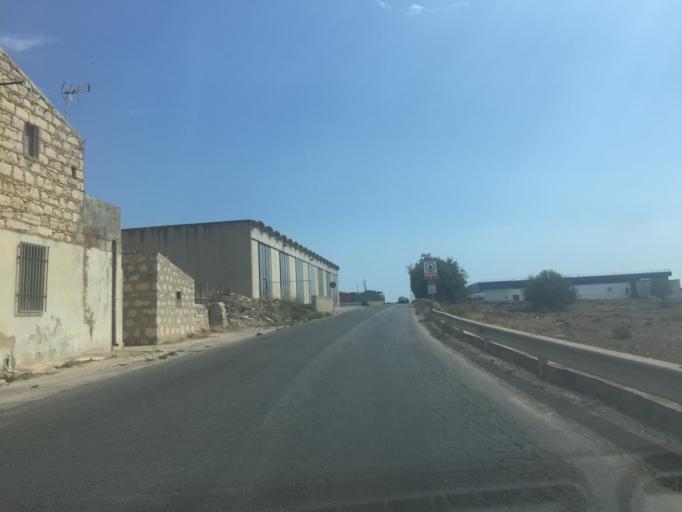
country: IT
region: Sicily
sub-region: Ragusa
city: Santa Croce Camerina
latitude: 36.8277
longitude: 14.5192
